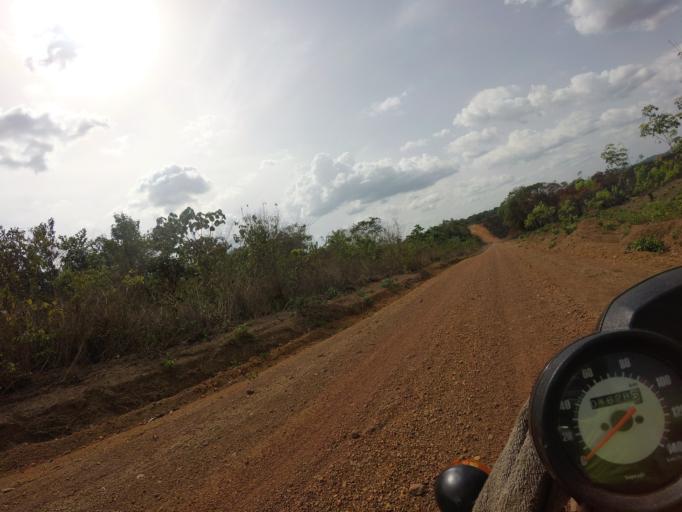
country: SL
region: Southern Province
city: Zimmi
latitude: 7.2411
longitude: -11.2013
